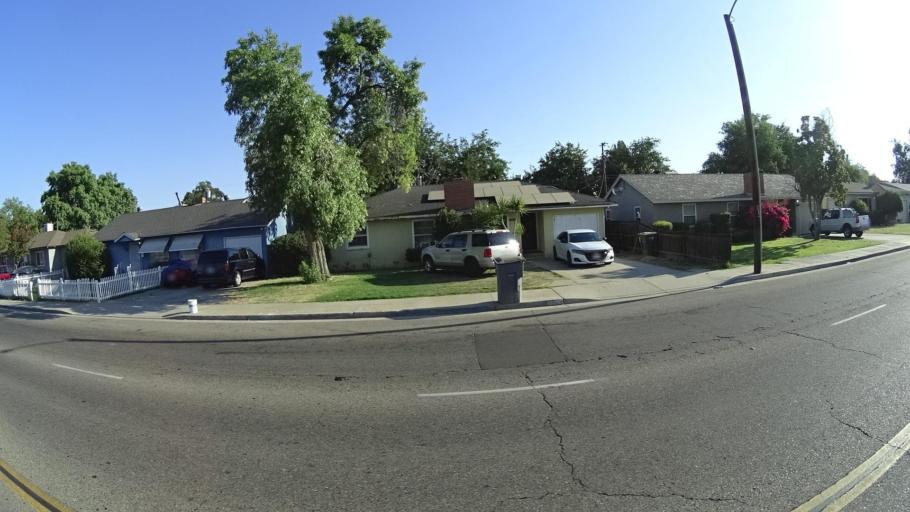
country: US
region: California
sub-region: Fresno County
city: Fresno
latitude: 36.7723
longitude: -119.7620
